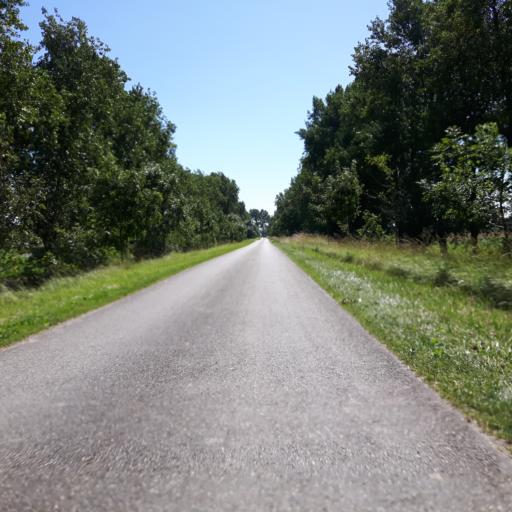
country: NL
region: Zeeland
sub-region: Gemeente Goes
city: Goes
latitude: 51.5669
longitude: 3.8115
